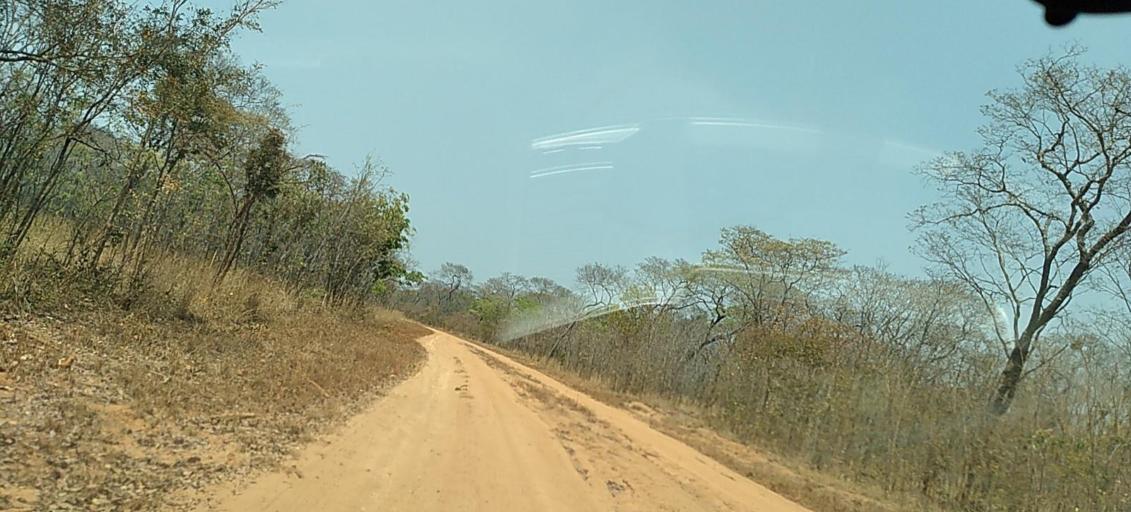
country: ZM
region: Central
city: Mumbwa
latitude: -14.3789
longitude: 26.4808
